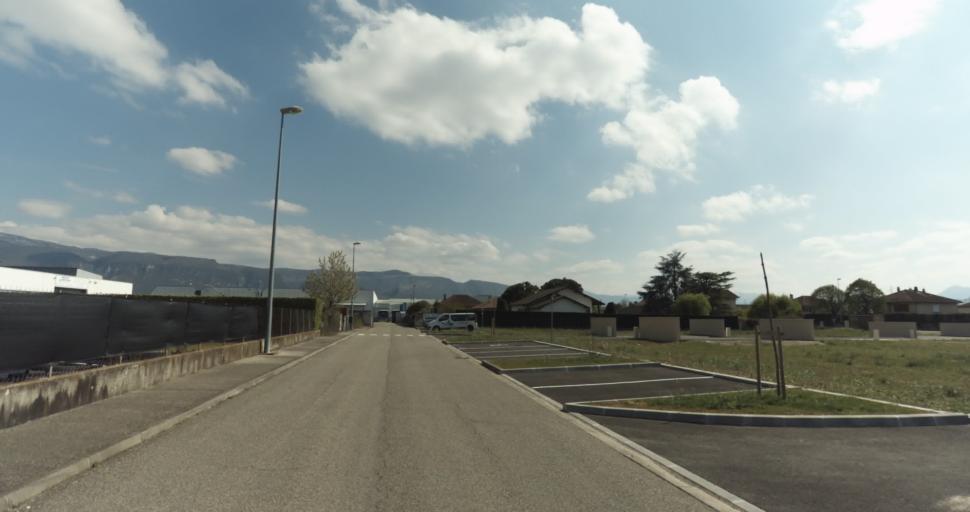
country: FR
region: Rhone-Alpes
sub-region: Departement de l'Isere
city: Saint-Marcellin
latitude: 45.1462
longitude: 5.3128
